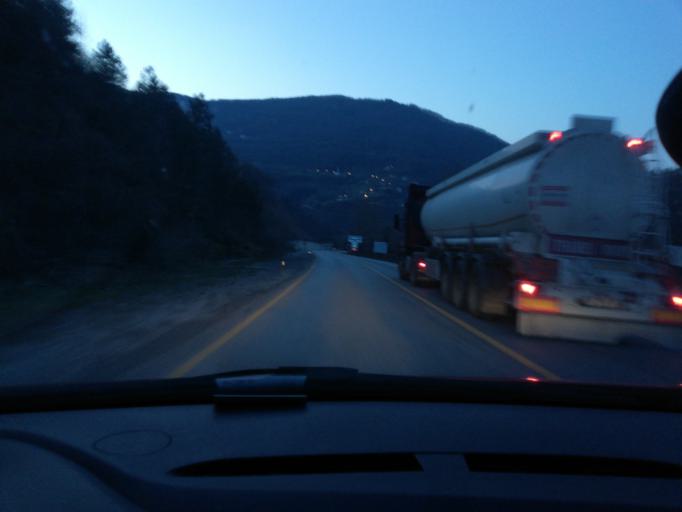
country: TR
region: Kastamonu
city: Inebolu
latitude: 41.9505
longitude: 33.7560
